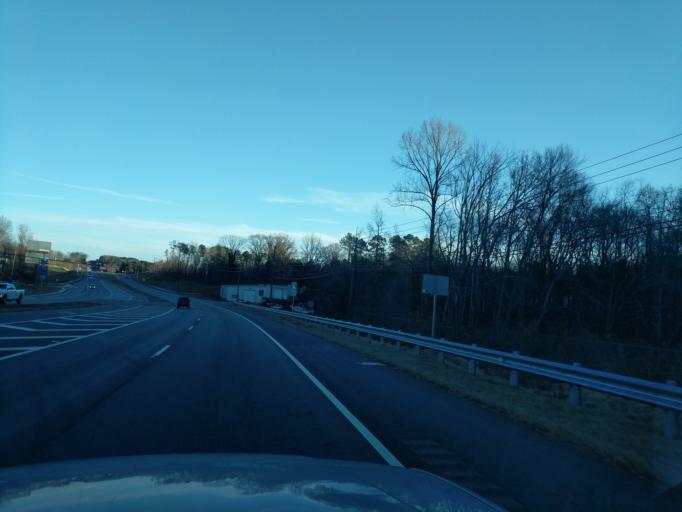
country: US
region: Georgia
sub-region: Stephens County
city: Toccoa
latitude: 34.5249
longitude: -83.2485
